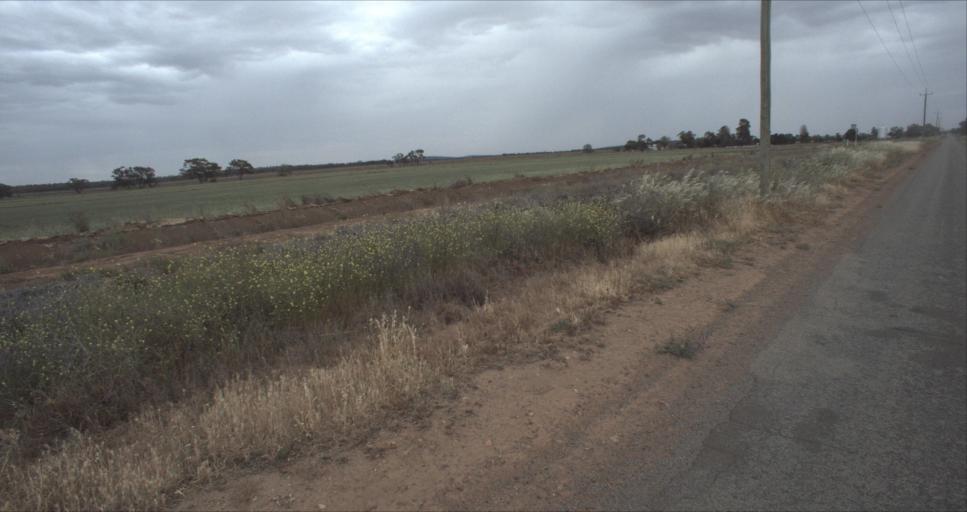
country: AU
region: New South Wales
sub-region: Leeton
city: Leeton
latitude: -34.4259
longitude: 146.3376
